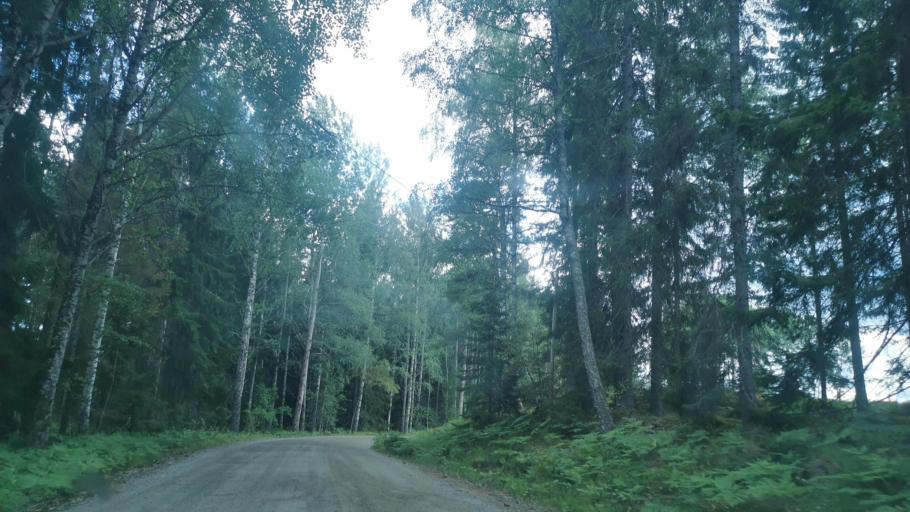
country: SE
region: OEstergoetland
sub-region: Finspangs Kommun
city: Finspang
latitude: 58.7890
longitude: 15.7672
